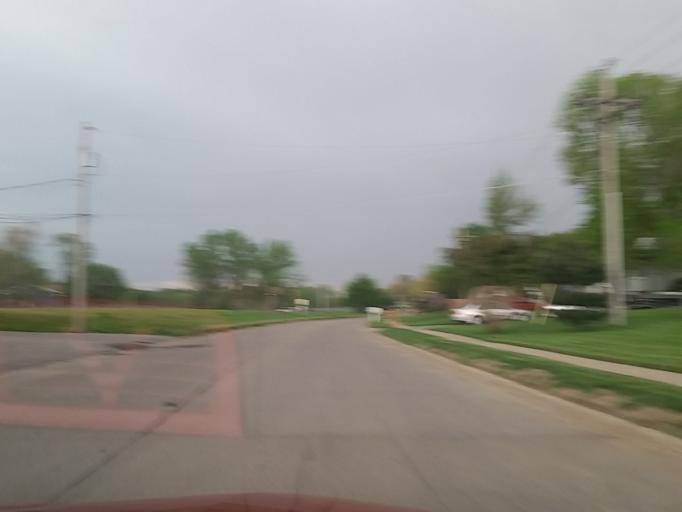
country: US
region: Nebraska
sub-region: Sarpy County
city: Offutt Air Force Base
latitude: 41.1487
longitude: -95.9190
